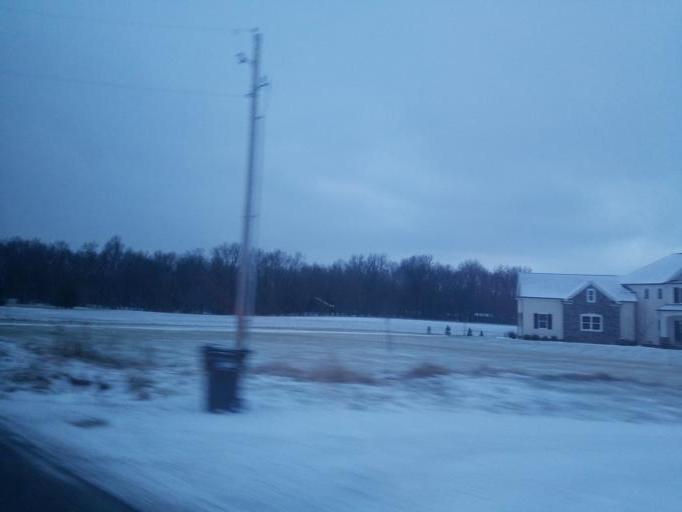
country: US
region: Ohio
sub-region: Delaware County
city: Sunbury
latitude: 40.2111
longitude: -82.8579
